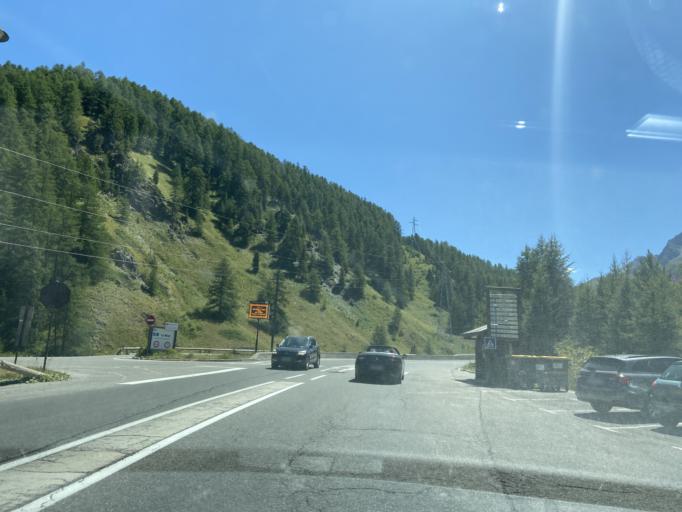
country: FR
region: Provence-Alpes-Cote d'Azur
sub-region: Departement des Hautes-Alpes
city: Guillestre
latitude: 44.5809
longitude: 6.6842
